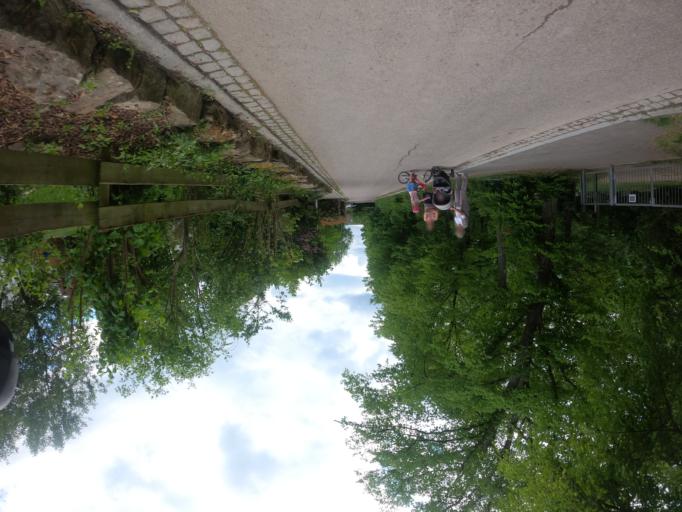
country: DE
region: Baden-Wuerttemberg
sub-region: Regierungsbezirk Stuttgart
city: Holzgerlingen
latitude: 48.6499
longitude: 9.0151
